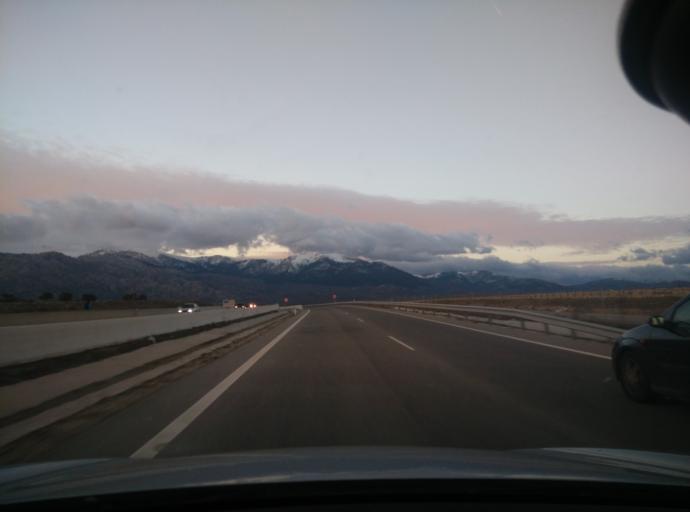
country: ES
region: Madrid
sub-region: Provincia de Madrid
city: Colmenar Viejo
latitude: 40.6979
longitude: -3.7892
